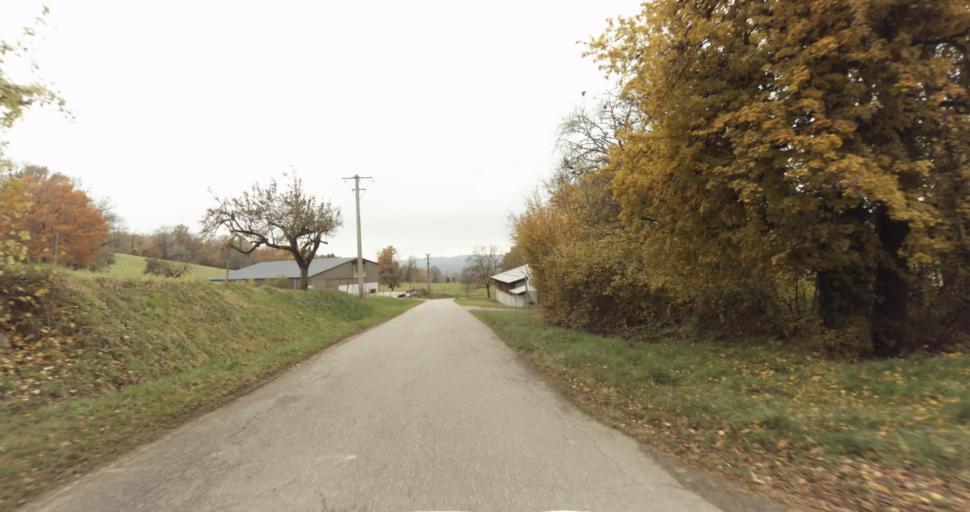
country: FR
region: Rhone-Alpes
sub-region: Departement de la Haute-Savoie
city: Chavanod
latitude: 45.8669
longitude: 6.0424
